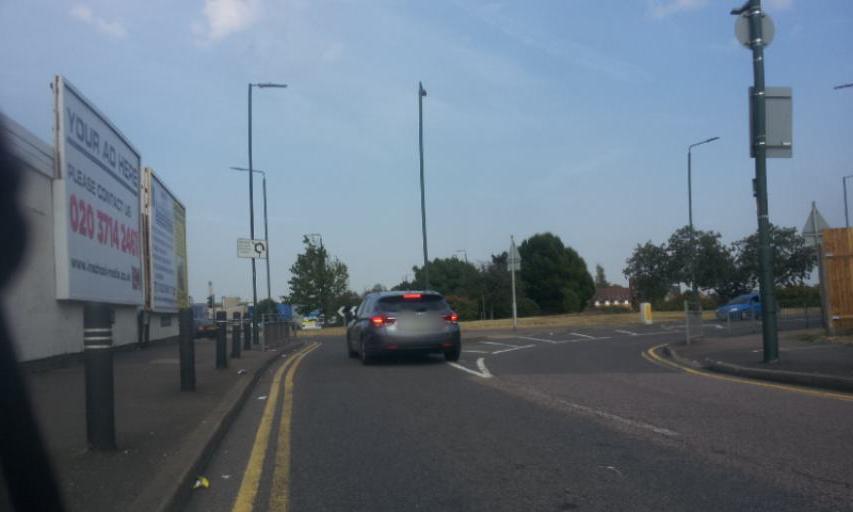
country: GB
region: England
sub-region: Greater London
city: Erith
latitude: 51.4636
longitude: 0.1815
